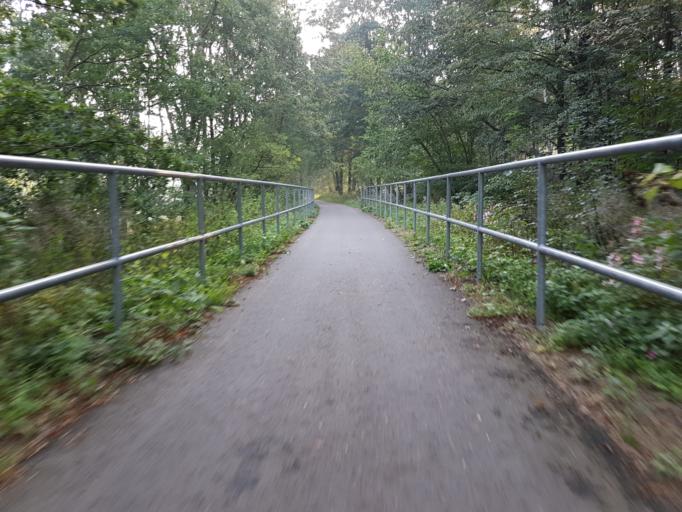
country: DE
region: Saxony
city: Taura
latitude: 50.9155
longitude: 12.8600
